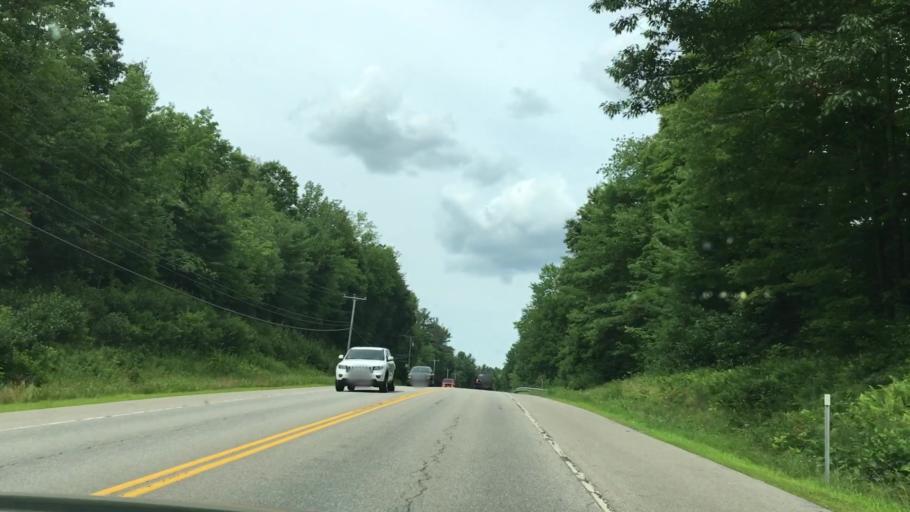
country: US
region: New Hampshire
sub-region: Cheshire County
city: Jaffrey
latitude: 42.8278
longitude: -71.9944
